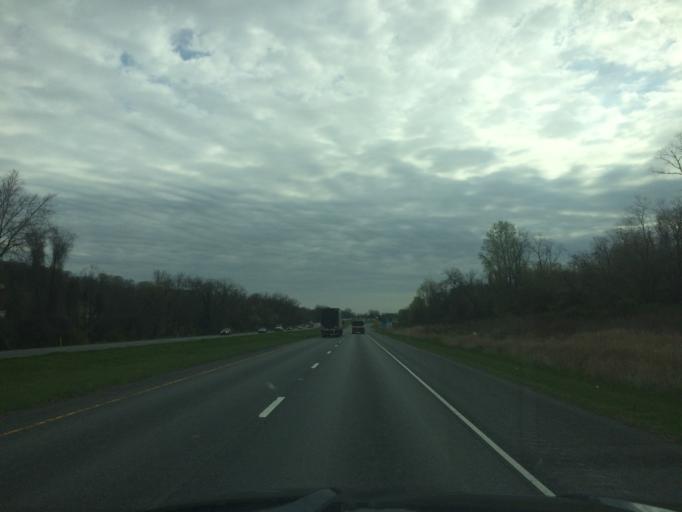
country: US
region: Pennsylvania
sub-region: York County
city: Hallam
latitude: 40.0031
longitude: -76.6258
